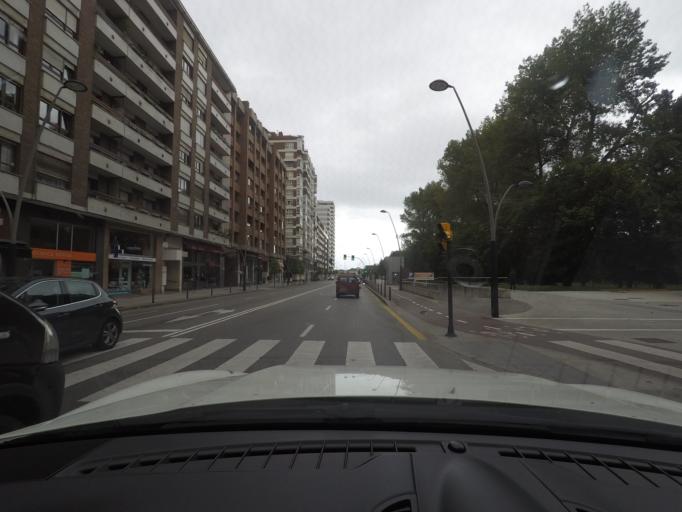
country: ES
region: Asturias
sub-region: Province of Asturias
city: Gijon
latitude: 43.5378
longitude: -5.6466
